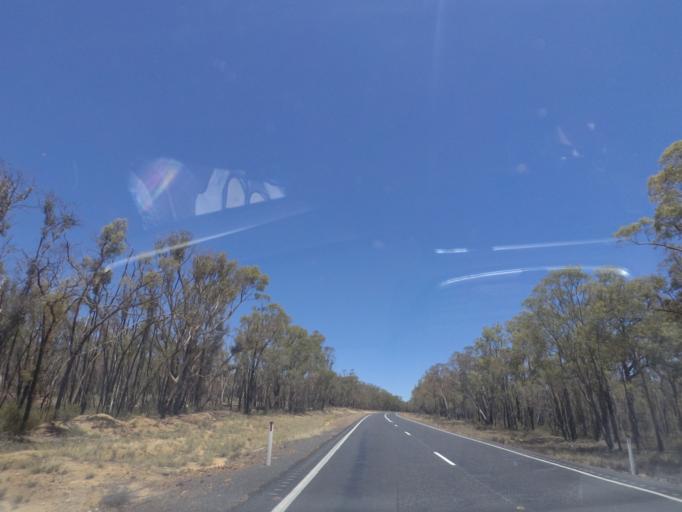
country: AU
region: New South Wales
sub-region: Warrumbungle Shire
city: Coonabarabran
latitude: -31.1866
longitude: 149.3547
